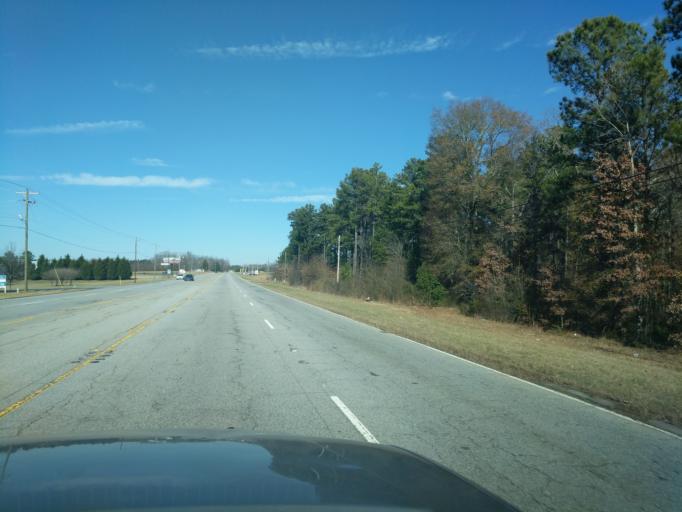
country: US
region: South Carolina
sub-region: Spartanburg County
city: Mayo
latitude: 35.1010
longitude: -81.8554
